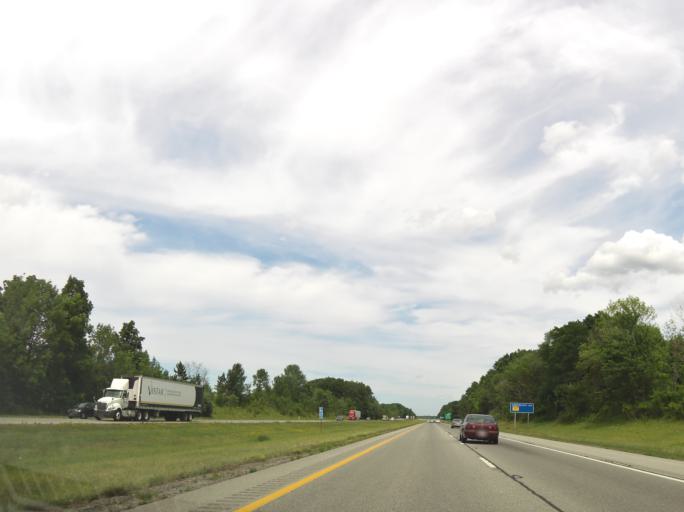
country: US
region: Ohio
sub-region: Lake County
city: Madison
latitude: 41.7495
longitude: -81.0714
